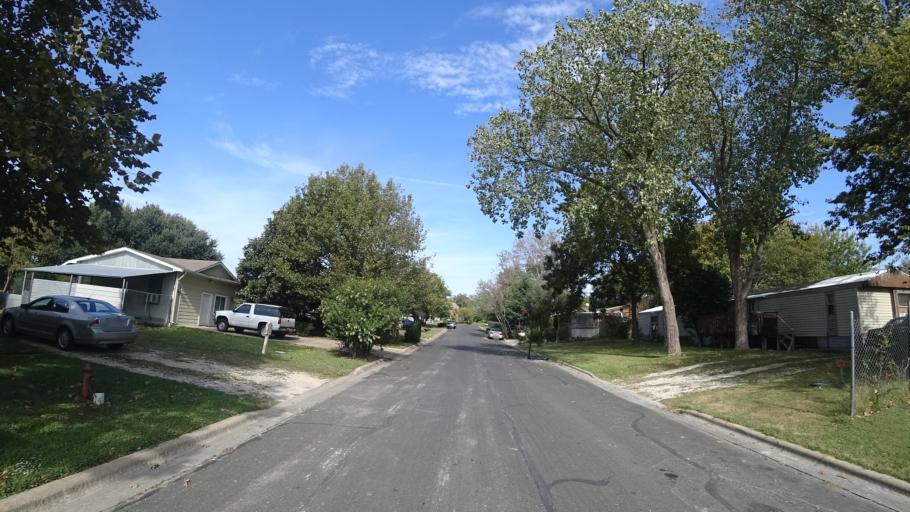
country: US
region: Texas
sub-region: Travis County
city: Pflugerville
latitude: 30.4112
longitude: -97.6325
